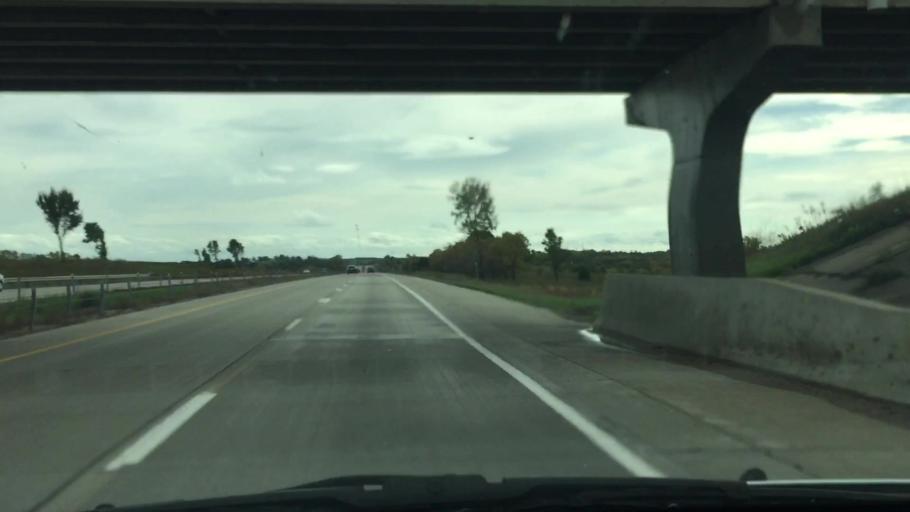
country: US
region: Iowa
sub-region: Clarke County
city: Osceola
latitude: 41.2533
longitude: -93.7810
